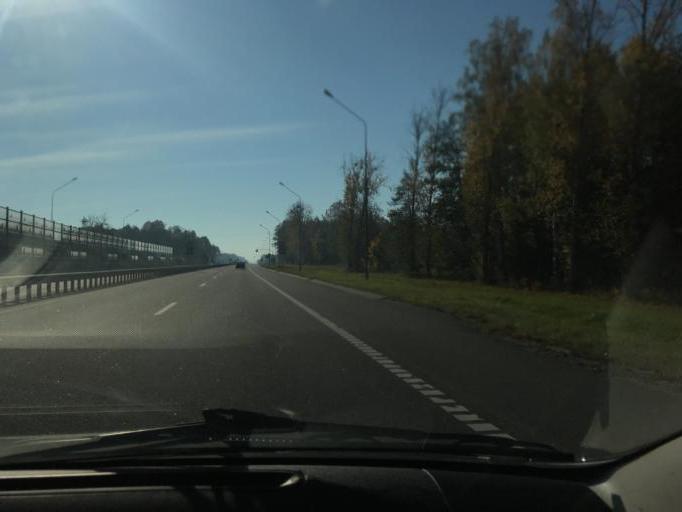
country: BY
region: Minsk
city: Slutsk
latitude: 53.2781
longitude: 27.5499
